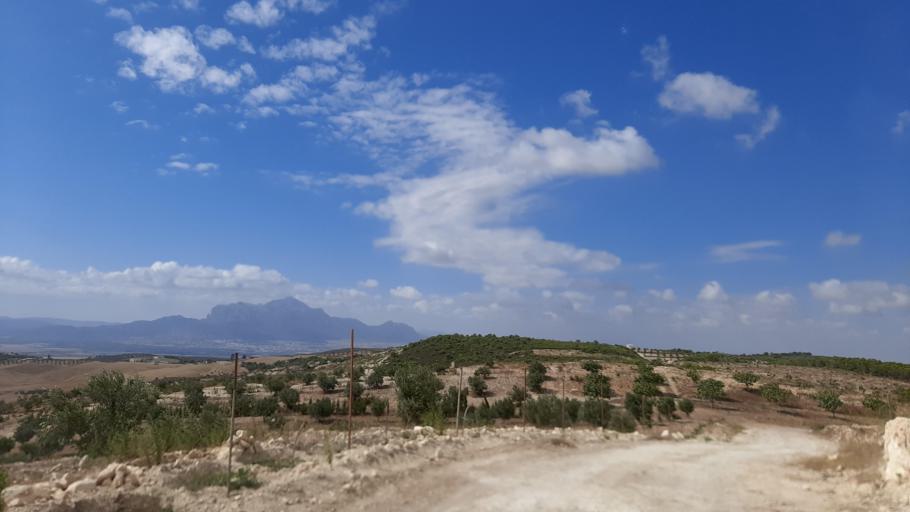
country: TN
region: Zaghwan
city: Zaghouan
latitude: 36.5016
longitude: 10.1812
